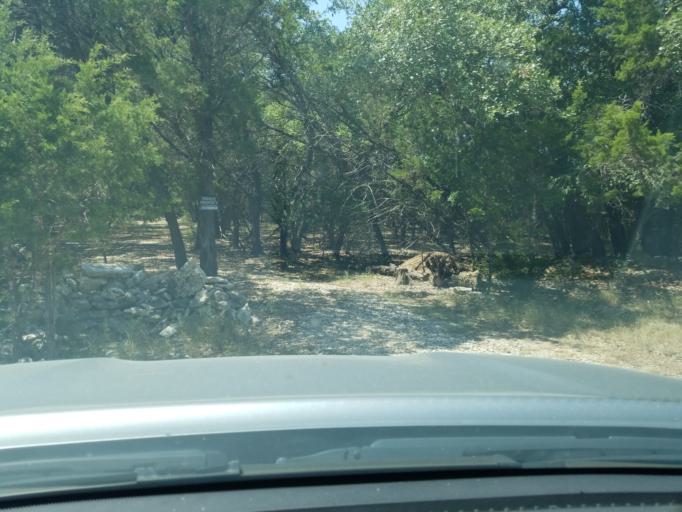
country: US
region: Texas
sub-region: Bexar County
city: Timberwood Park
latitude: 29.7173
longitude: -98.4937
